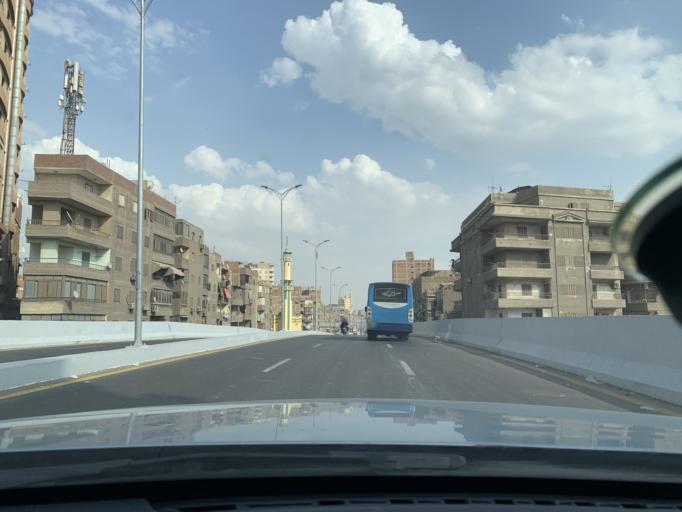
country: EG
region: Muhafazat al Qahirah
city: Cairo
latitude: 30.1262
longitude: 31.2979
